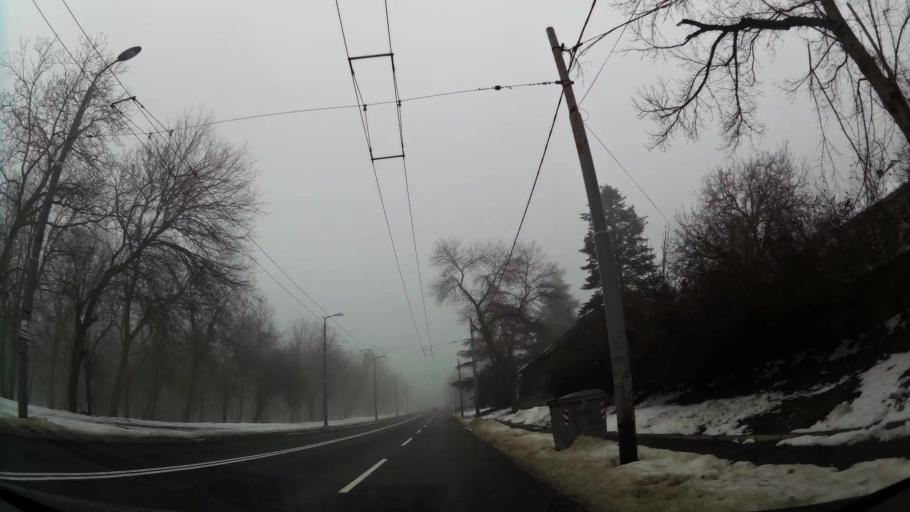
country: RS
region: Central Serbia
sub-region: Belgrade
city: Savski Venac
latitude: 44.7850
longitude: 20.4576
